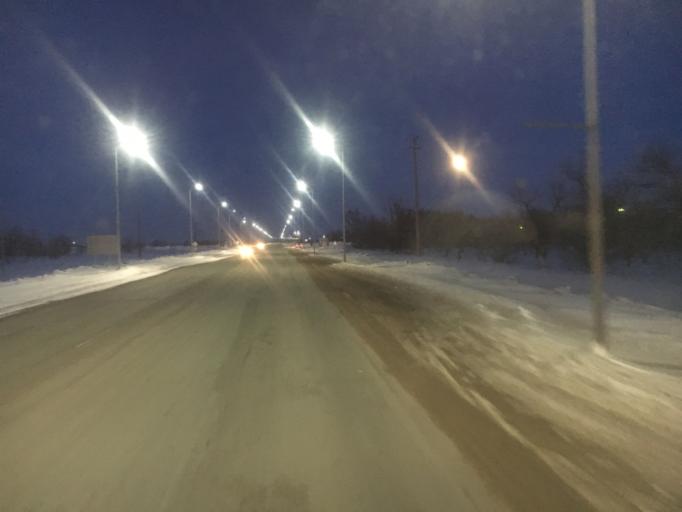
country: KZ
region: Batys Qazaqstan
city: Oral
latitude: 51.1575
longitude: 51.4989
